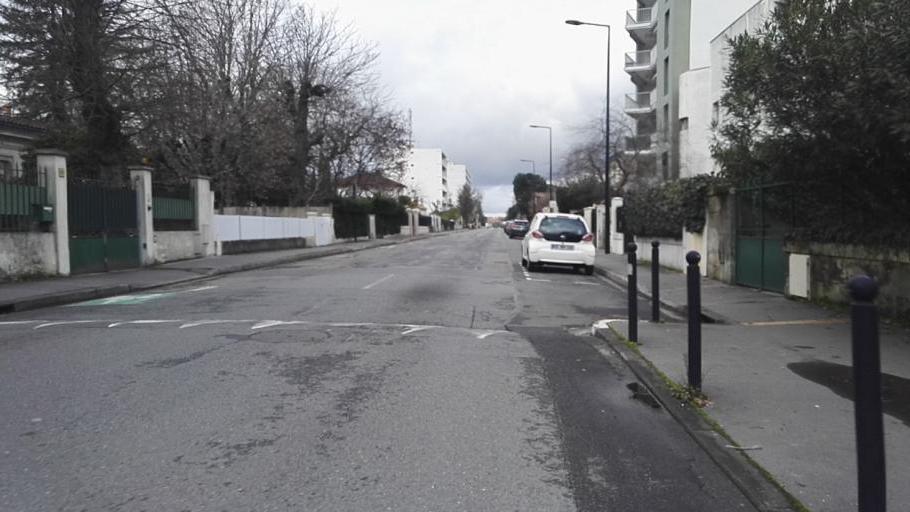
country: FR
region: Aquitaine
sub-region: Departement de la Gironde
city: Le Bouscat
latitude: 44.8562
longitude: -0.6137
